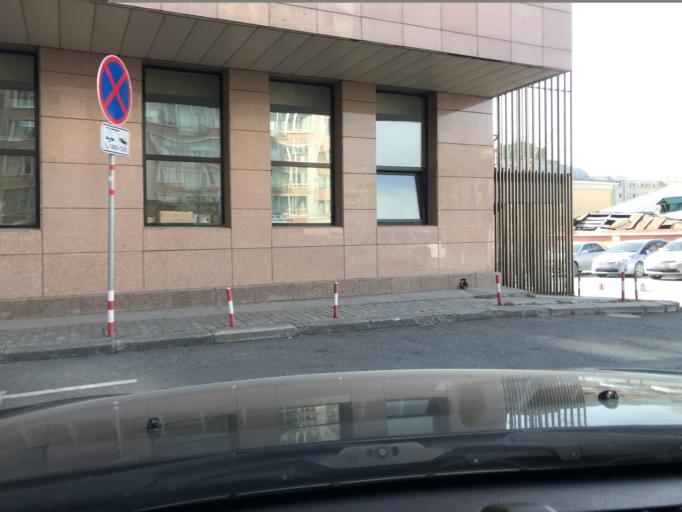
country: MN
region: Ulaanbaatar
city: Ulaanbaatar
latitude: 47.9208
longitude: 106.9101
